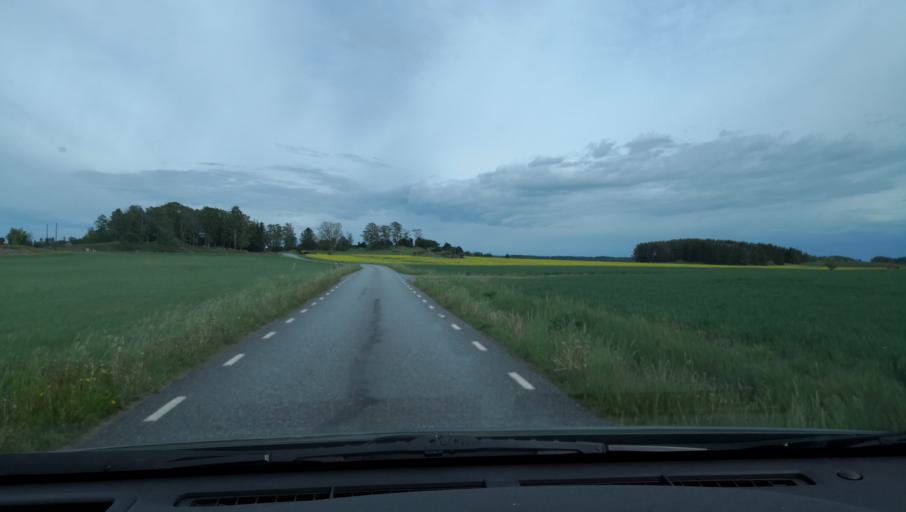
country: SE
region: Uppsala
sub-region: Enkopings Kommun
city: Orsundsbro
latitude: 59.7053
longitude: 17.3654
